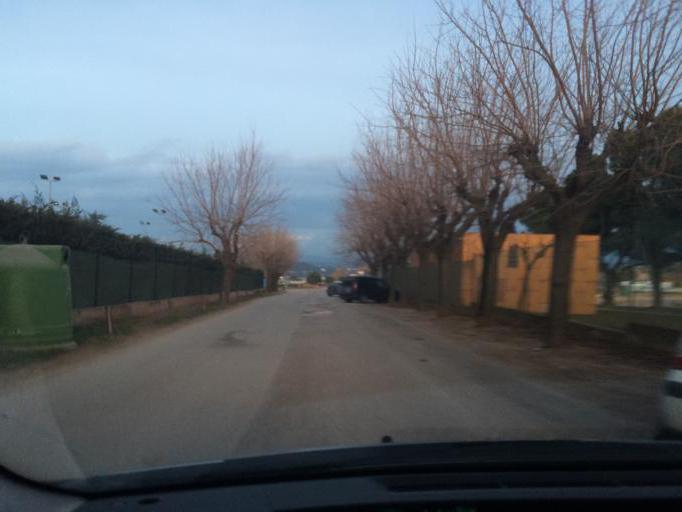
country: ES
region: Catalonia
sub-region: Provincia de Barcelona
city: Sant Fruitos de Bages
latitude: 41.7500
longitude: 1.8439
